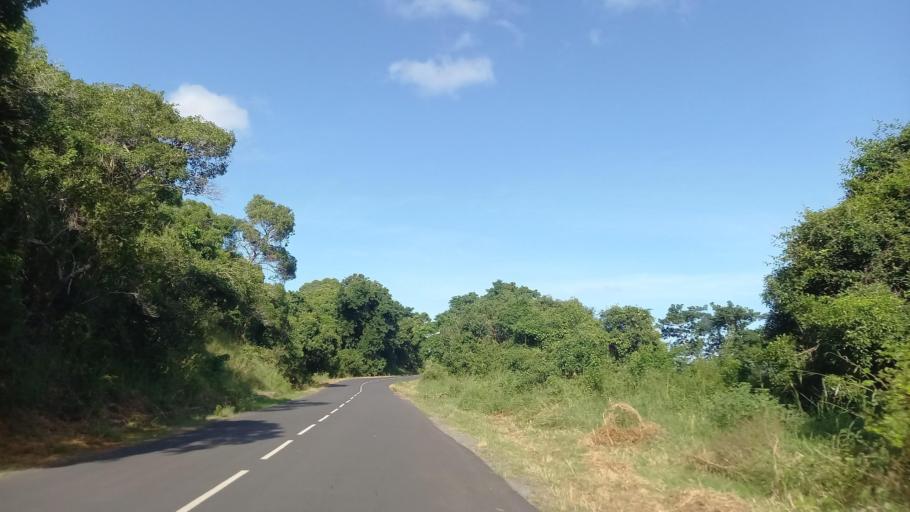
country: YT
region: Kani-Keli
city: Kani Keli
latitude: -12.9720
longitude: 45.1108
